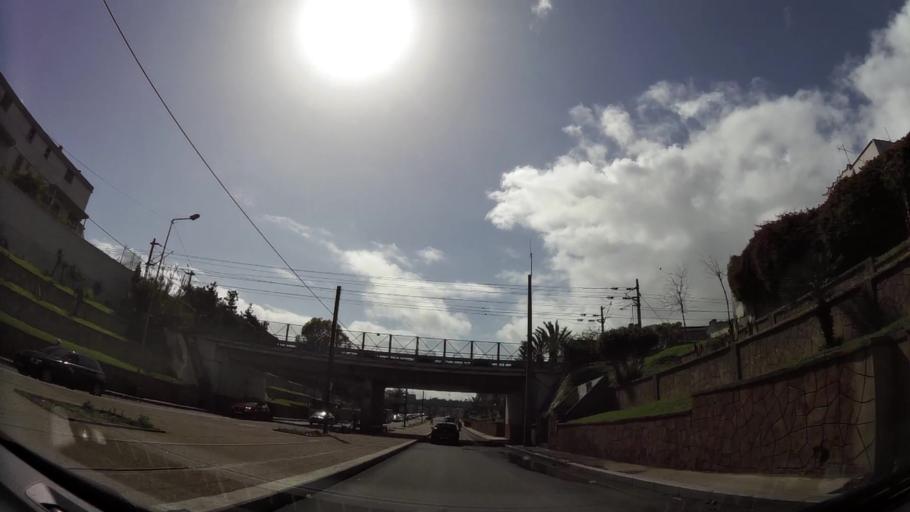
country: MA
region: Grand Casablanca
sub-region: Casablanca
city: Casablanca
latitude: 33.5682
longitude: -7.6109
